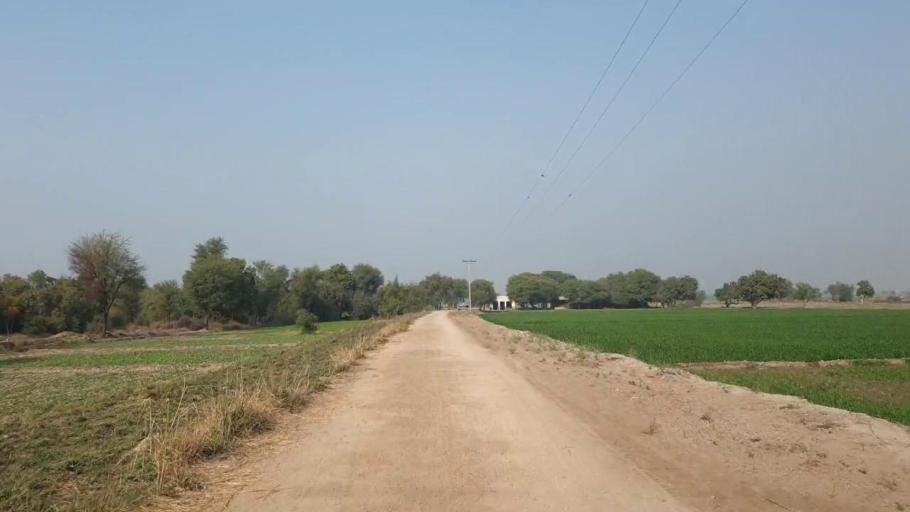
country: PK
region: Sindh
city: Shahdadpur
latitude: 26.0068
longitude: 68.5290
